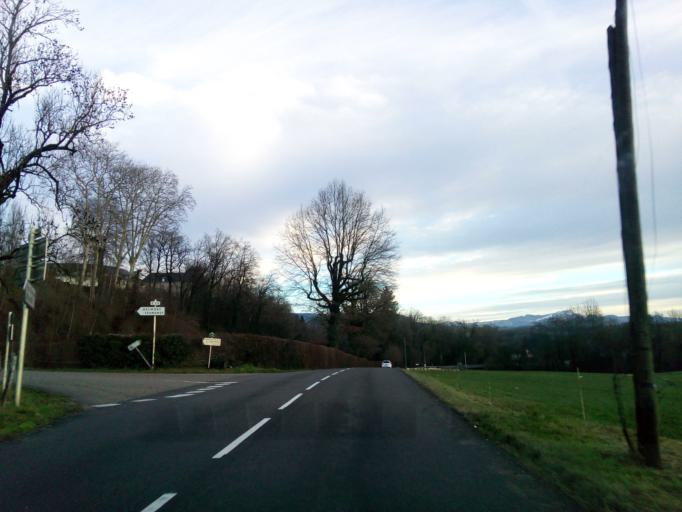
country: FR
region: Rhone-Alpes
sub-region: Departement de la Savoie
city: Le Pont-de-Beauvoisin
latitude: 45.5613
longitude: 5.6744
